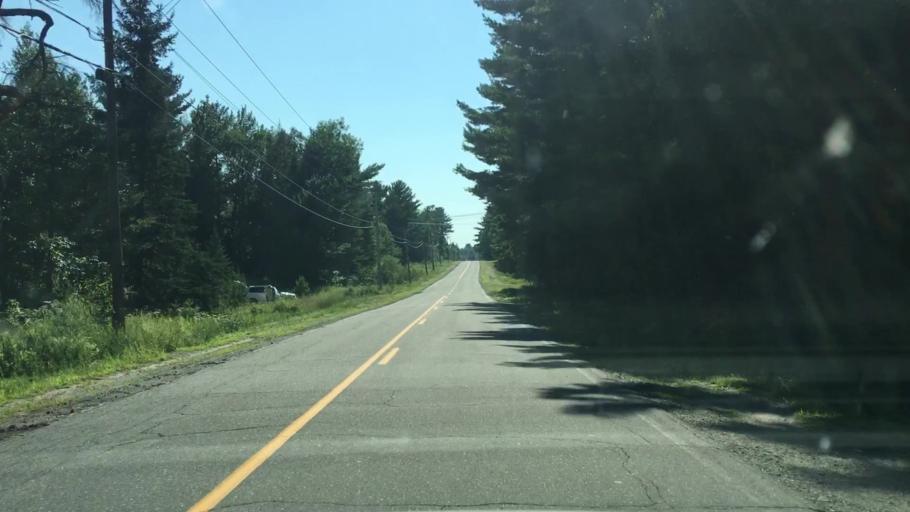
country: US
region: Maine
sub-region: Penobscot County
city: Enfield
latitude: 45.2465
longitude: -68.5991
